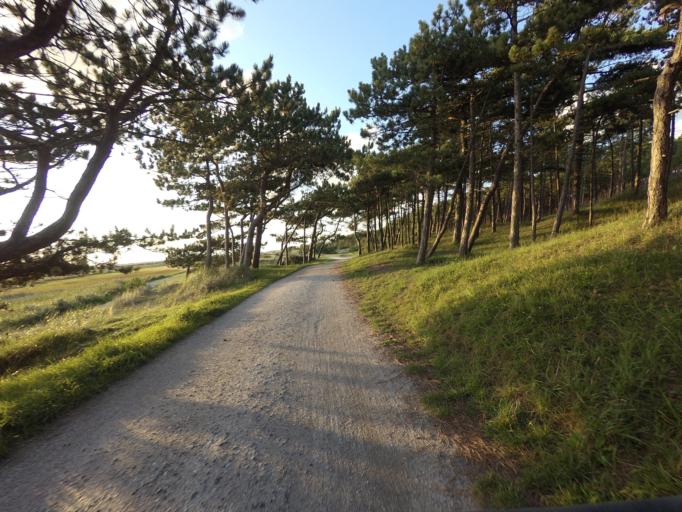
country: NL
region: Friesland
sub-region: Gemeente Terschelling
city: West-Terschelling
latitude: 53.3581
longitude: 5.2093
